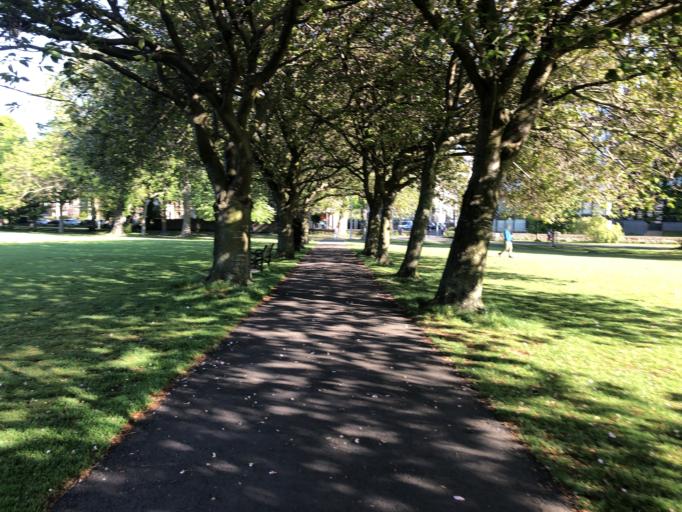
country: GB
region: Scotland
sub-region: Edinburgh
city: Edinburgh
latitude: 55.9418
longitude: -3.1961
